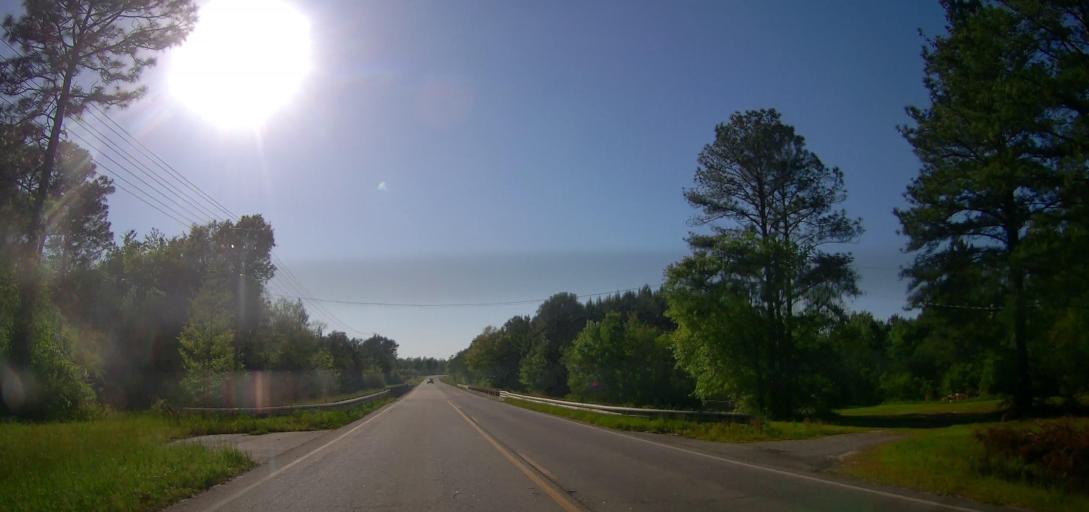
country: US
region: Georgia
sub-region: Ben Hill County
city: Fitzgerald
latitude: 31.6938
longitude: -83.2908
